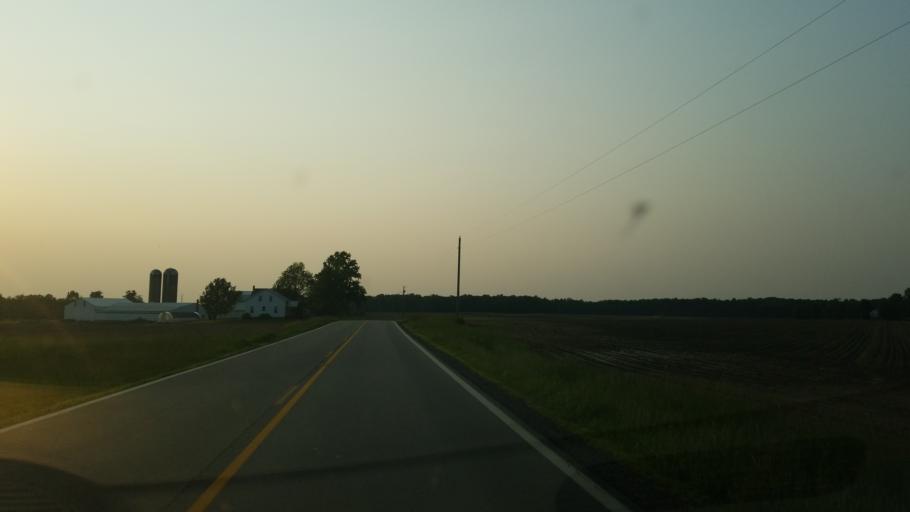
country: US
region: Ohio
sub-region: Ashland County
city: Ashland
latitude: 40.9542
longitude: -82.3350
